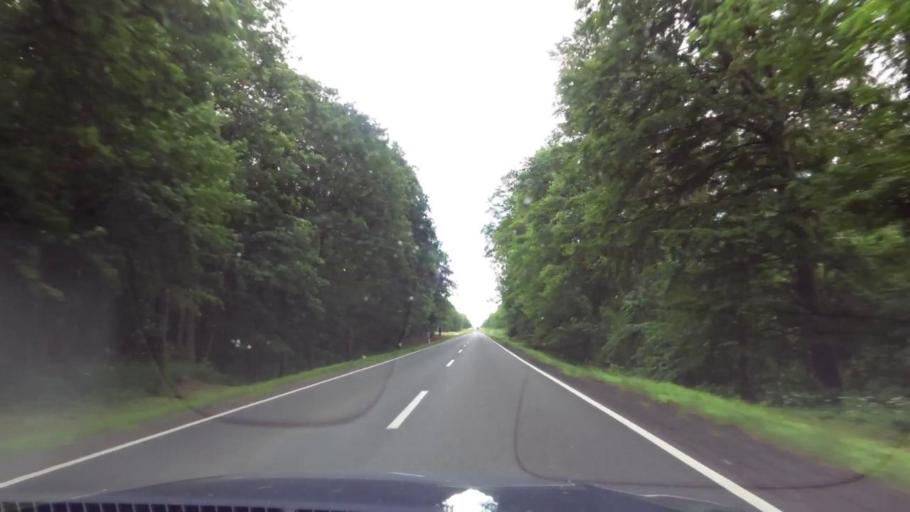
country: PL
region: West Pomeranian Voivodeship
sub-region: Powiat mysliborski
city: Mysliborz
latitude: 52.9672
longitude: 14.7447
